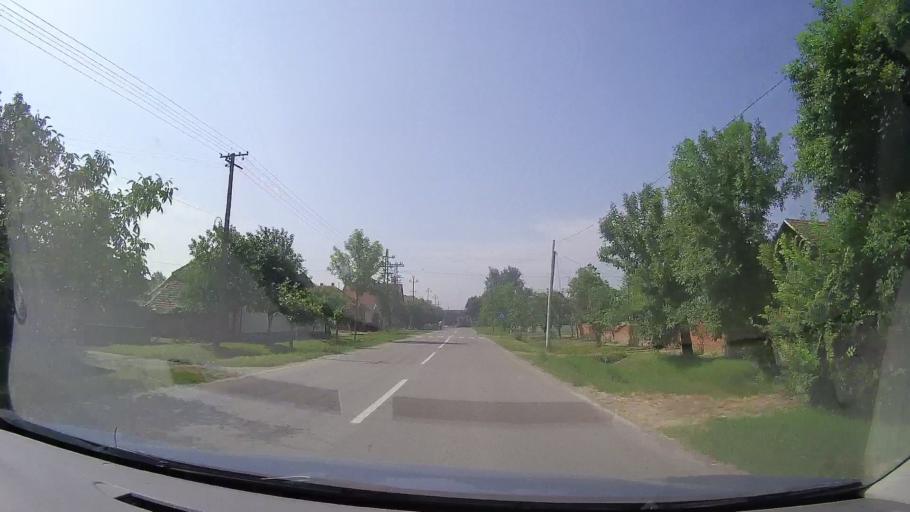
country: RS
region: Autonomna Pokrajina Vojvodina
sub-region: Srednjebanatski Okrug
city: Secanj
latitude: 45.3699
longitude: 20.7772
